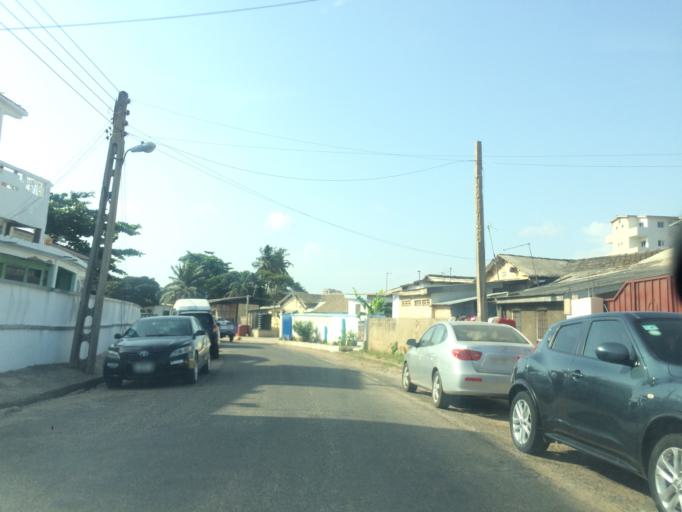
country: GH
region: Greater Accra
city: Accra
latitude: 5.5575
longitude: -0.1773
